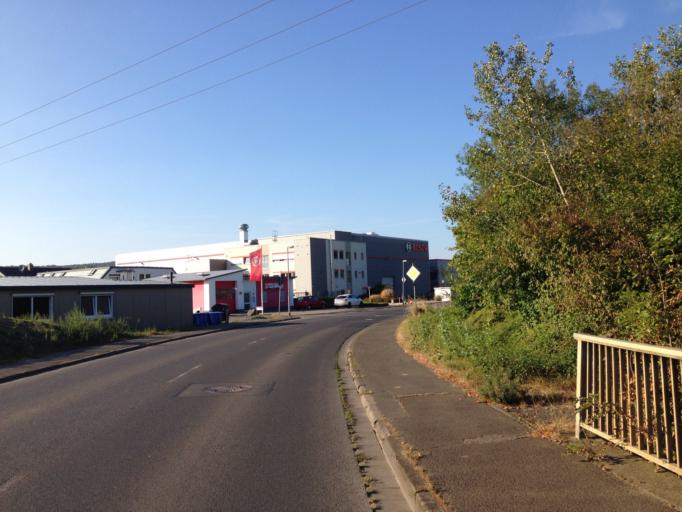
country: DE
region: Hesse
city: Lollar
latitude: 50.6447
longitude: 8.6974
